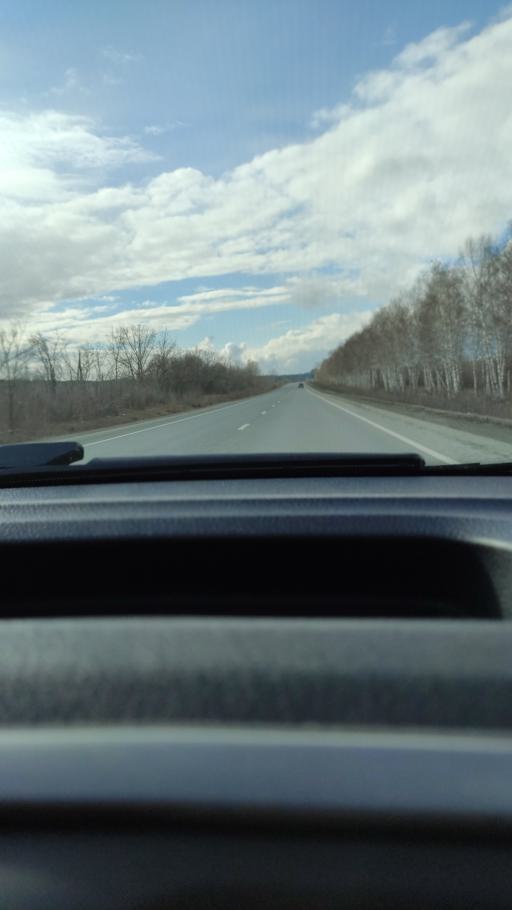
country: RU
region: Samara
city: Kurumoch
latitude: 53.4874
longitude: 50.0043
